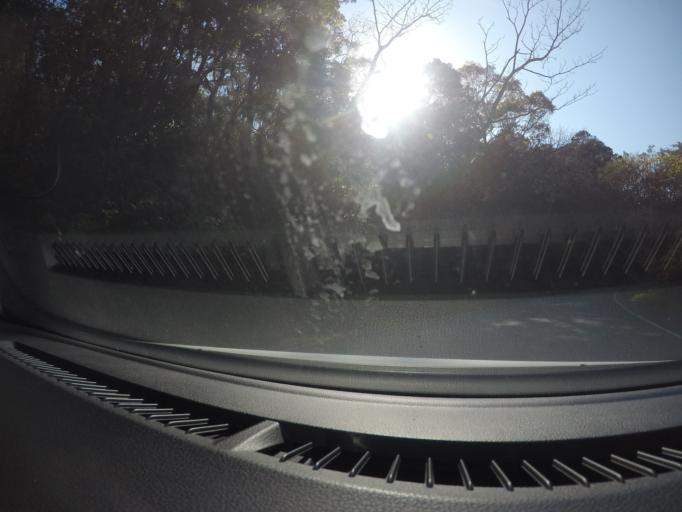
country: JP
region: Kochi
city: Kochi-shi
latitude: 33.5489
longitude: 133.5756
